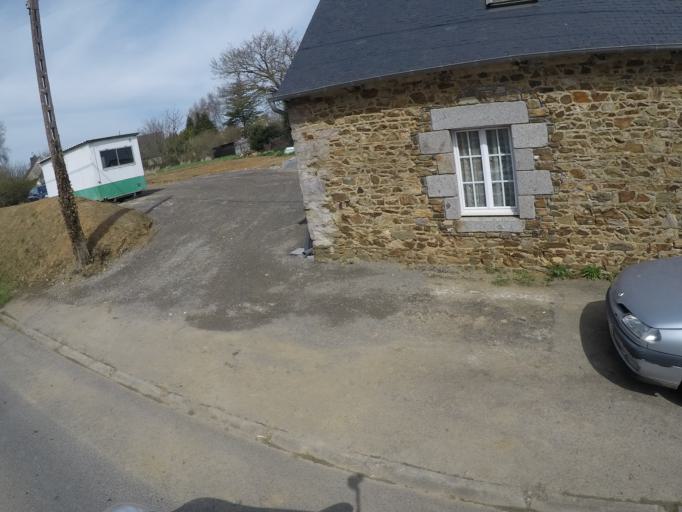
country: FR
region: Brittany
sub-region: Departement des Cotes-d'Armor
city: Plelo
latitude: 48.5780
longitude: -2.9201
